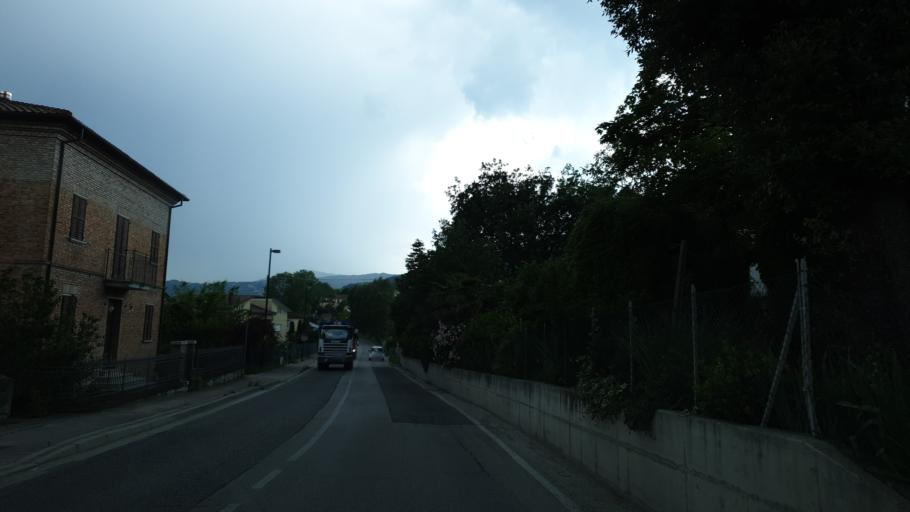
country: IT
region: Emilia-Romagna
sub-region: Provincia di Rimini
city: Secchiano
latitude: 43.9229
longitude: 12.3150
